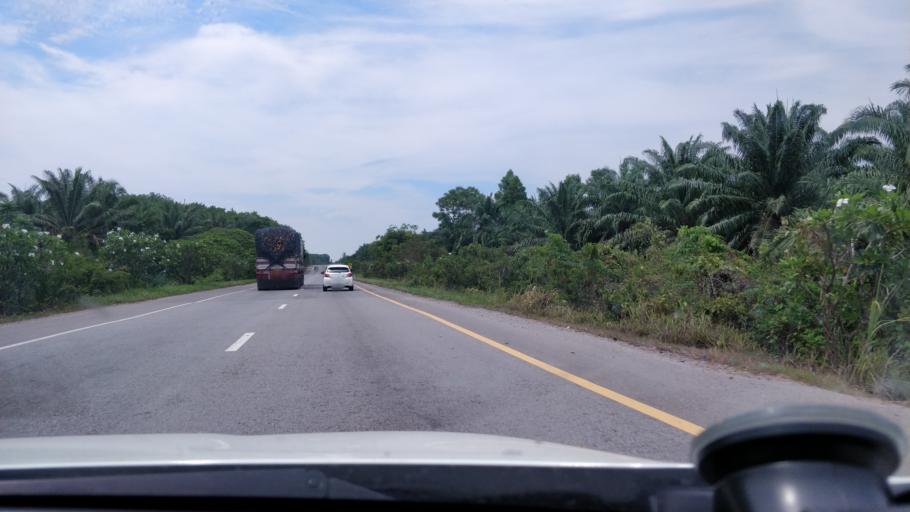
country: TH
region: Surat Thani
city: Khian Sa
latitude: 8.7863
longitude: 99.1615
